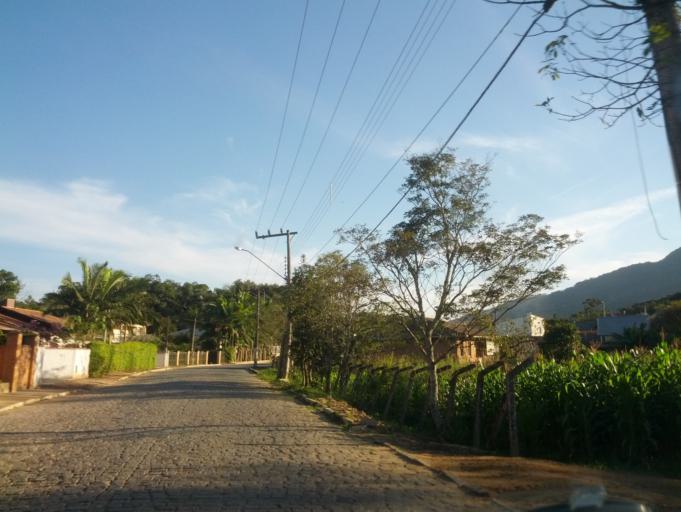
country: BR
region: Santa Catarina
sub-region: Indaial
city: Indaial
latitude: -26.9055
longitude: -49.2606
